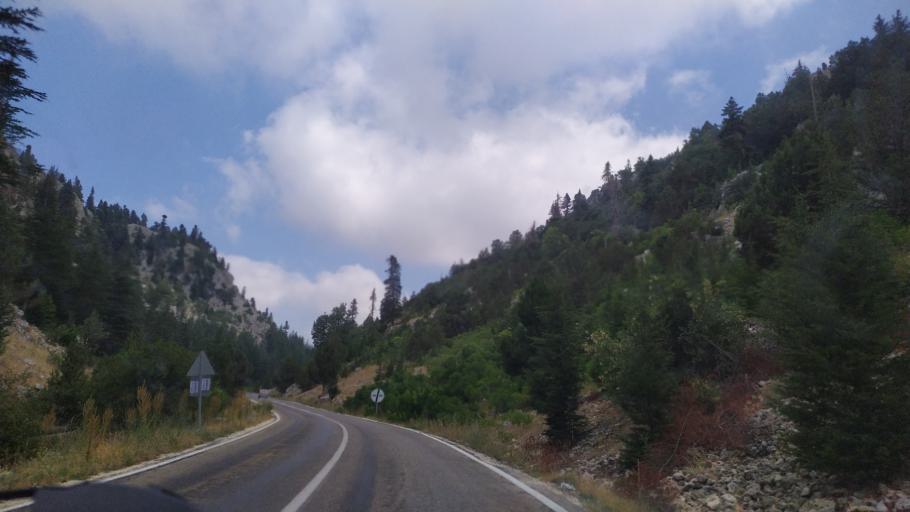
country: TR
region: Mersin
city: Kirobasi
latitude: 36.6080
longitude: 33.8835
